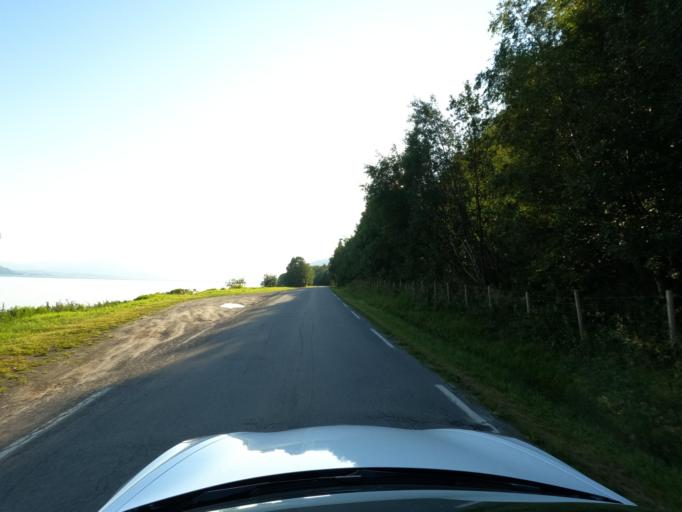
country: NO
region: Nordland
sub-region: Ballangen
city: Ballangen
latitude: 68.4684
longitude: 16.8416
